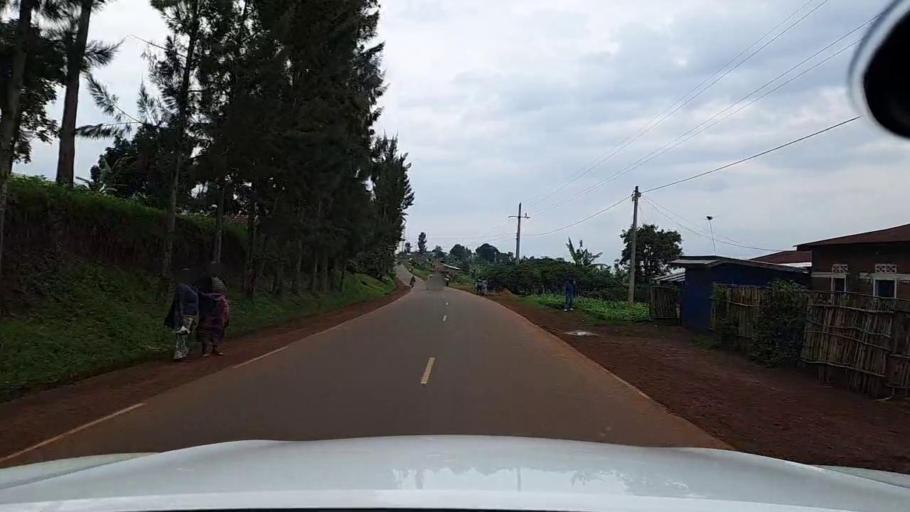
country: RW
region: Western Province
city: Cyangugu
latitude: -2.6212
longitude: 28.9463
